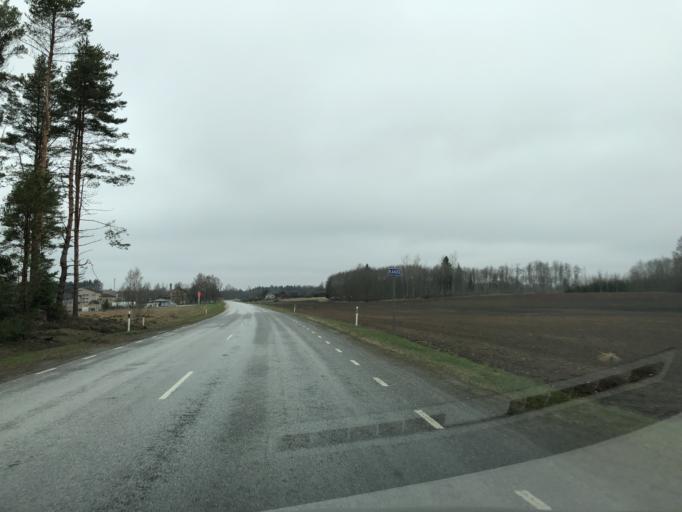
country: EE
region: Laeaene-Virumaa
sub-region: Rakke vald
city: Rakke
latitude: 58.9800
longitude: 26.2664
